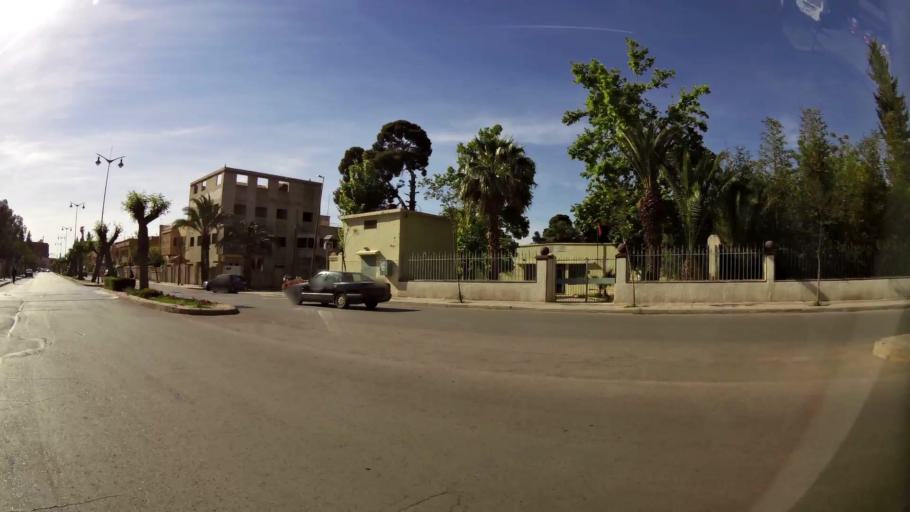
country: MA
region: Oriental
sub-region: Oujda-Angad
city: Oujda
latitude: 34.6715
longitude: -1.9078
